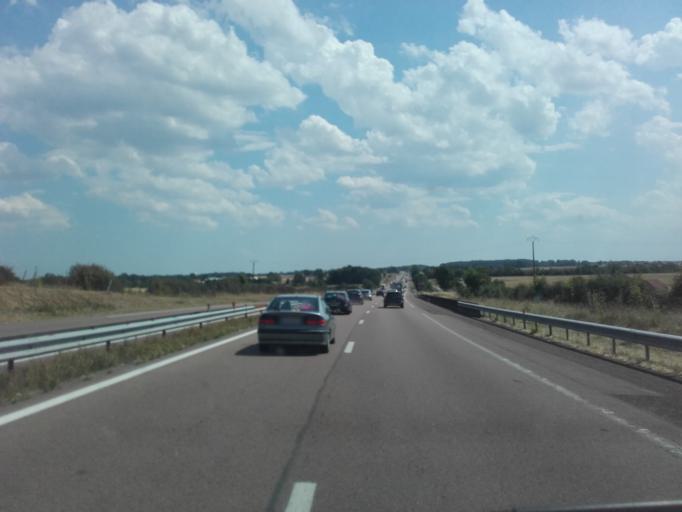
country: FR
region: Bourgogne
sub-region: Departement de l'Yonne
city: Avallon
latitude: 47.5458
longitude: 3.9695
